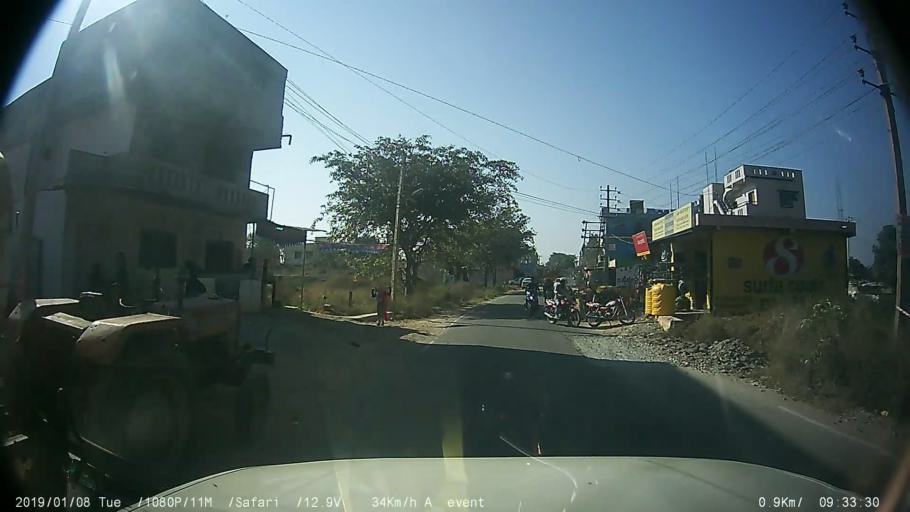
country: IN
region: Karnataka
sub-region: Bangalore Urban
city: Anekal
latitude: 12.8227
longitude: 77.6515
